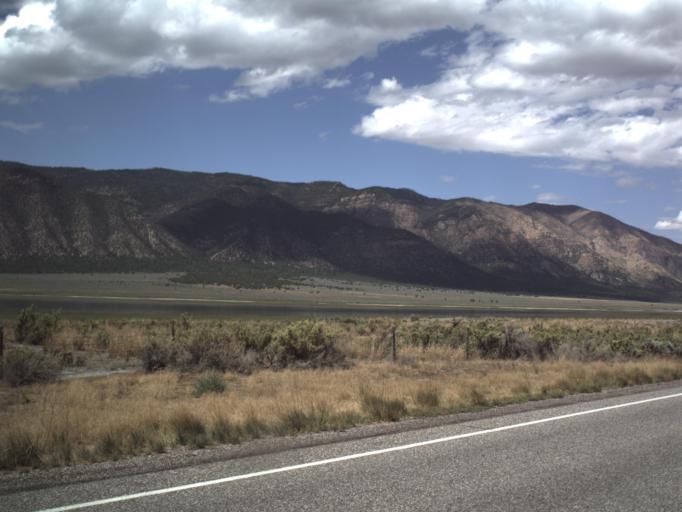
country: US
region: Utah
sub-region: Sevier County
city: Aurora
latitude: 39.1067
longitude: -112.0419
